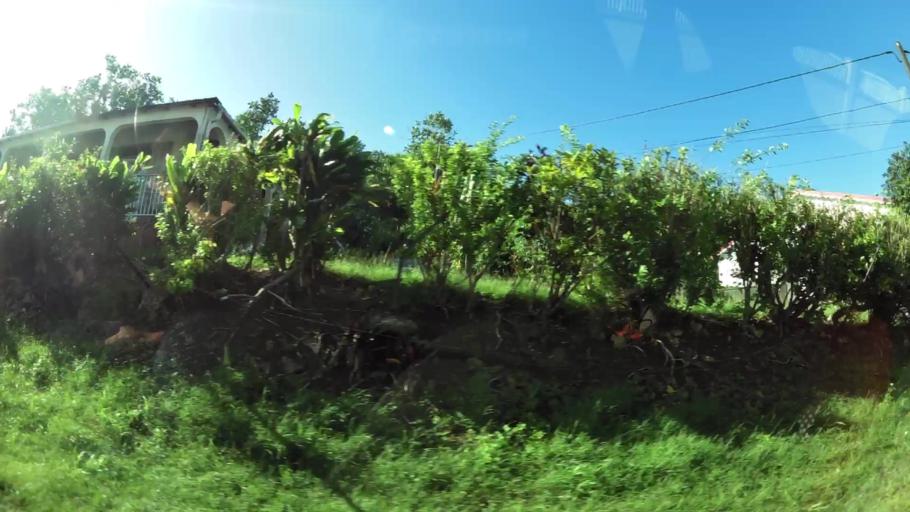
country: GP
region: Guadeloupe
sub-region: Guadeloupe
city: Petit-Canal
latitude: 16.3196
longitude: -61.4341
